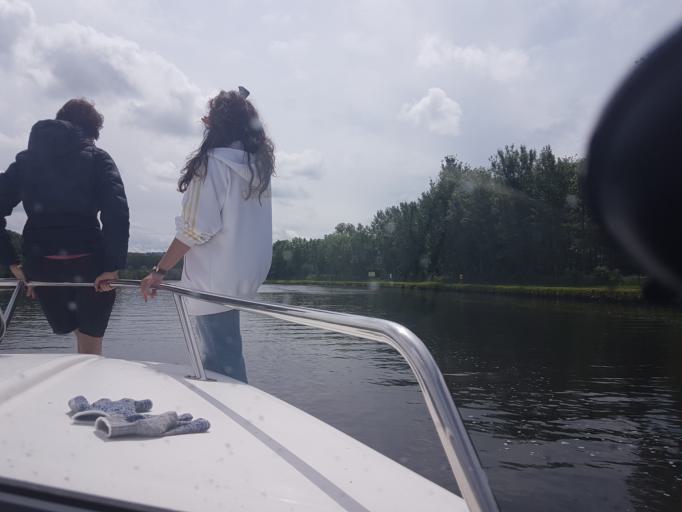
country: FR
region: Bourgogne
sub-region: Departement de l'Yonne
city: Augy
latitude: 47.7808
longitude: 3.6023
